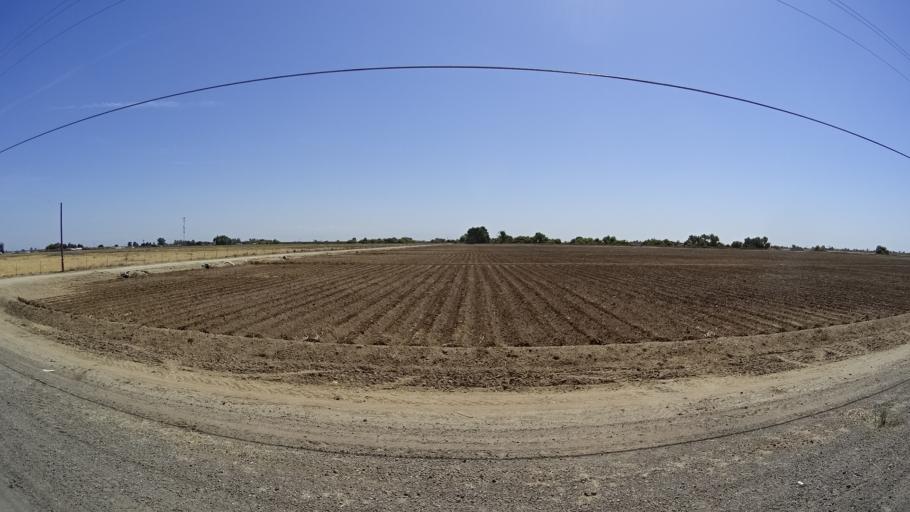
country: US
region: California
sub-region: Kings County
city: Lemoore
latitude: 36.2615
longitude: -119.7809
